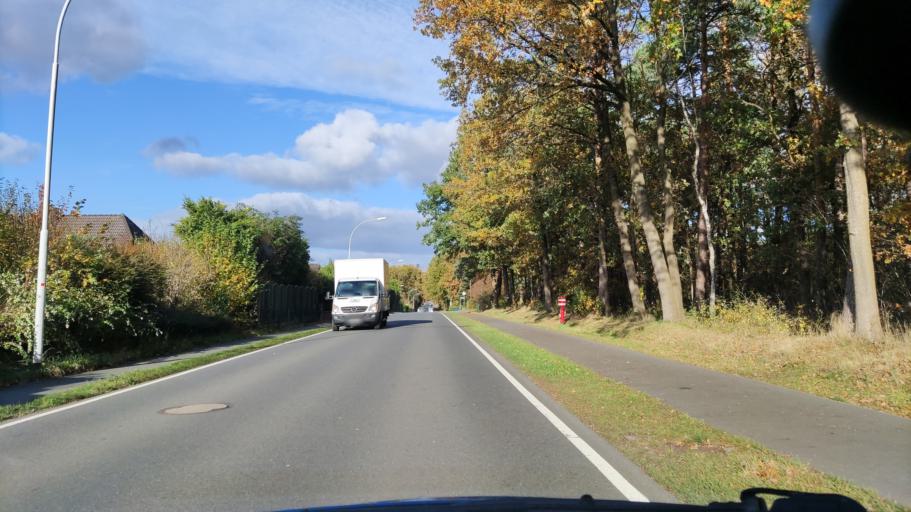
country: DE
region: Lower Saxony
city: Munster
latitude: 53.0055
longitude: 10.0883
